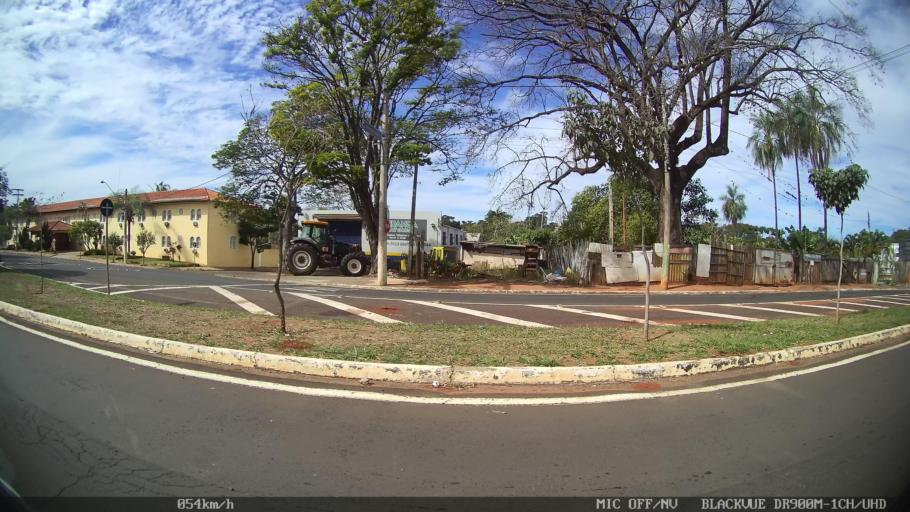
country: BR
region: Sao Paulo
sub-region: Catanduva
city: Catanduva
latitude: -21.1529
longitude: -48.9812
